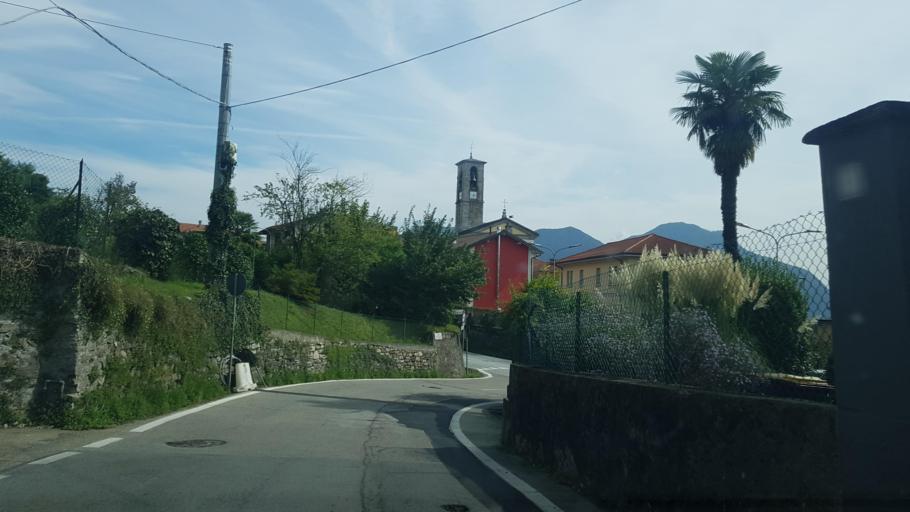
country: IT
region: Piedmont
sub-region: Provincia Verbano-Cusio-Ossola
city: Pallanza-Intra-Suna
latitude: 45.9469
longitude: 8.5742
